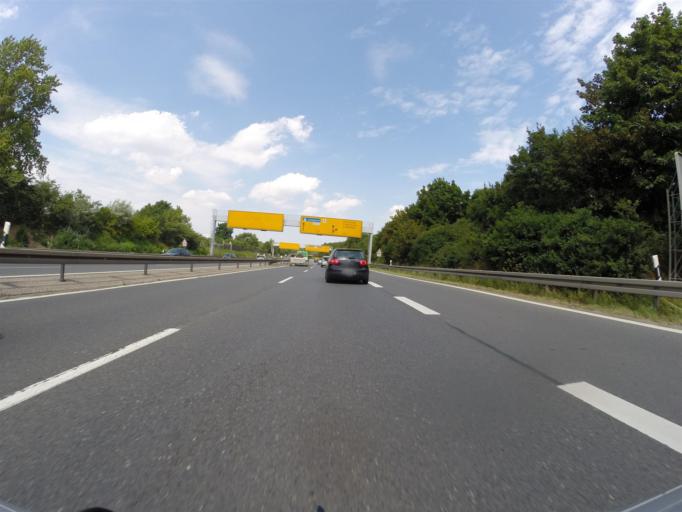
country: DE
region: Lower Saxony
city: Laatzen
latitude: 52.3336
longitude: 9.8104
